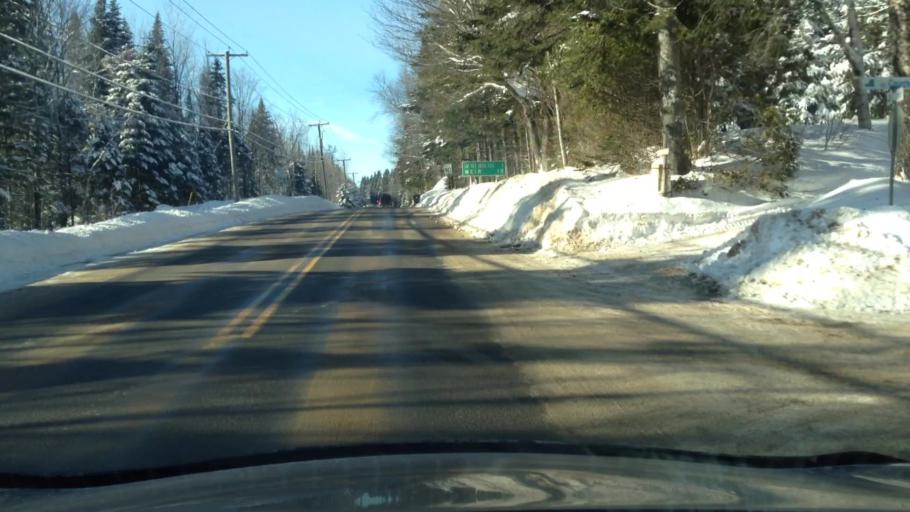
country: CA
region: Quebec
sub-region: Laurentides
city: Sainte-Agathe-des-Monts
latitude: 45.9276
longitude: -74.4016
